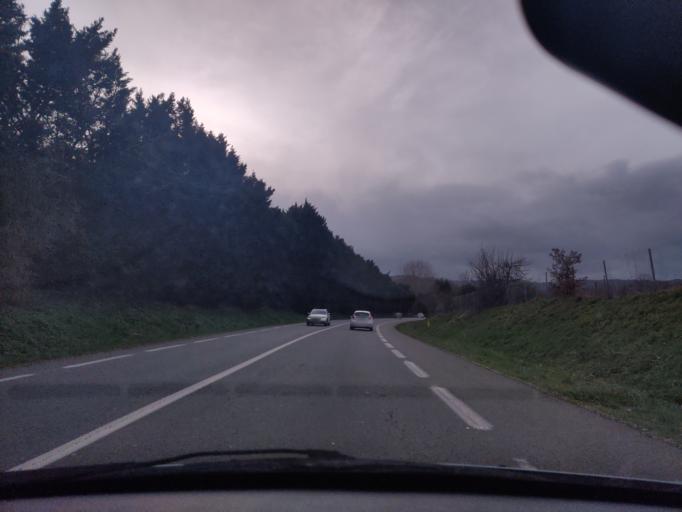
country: FR
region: Auvergne
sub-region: Departement du Puy-de-Dome
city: Mozac
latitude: 45.8820
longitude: 3.0919
